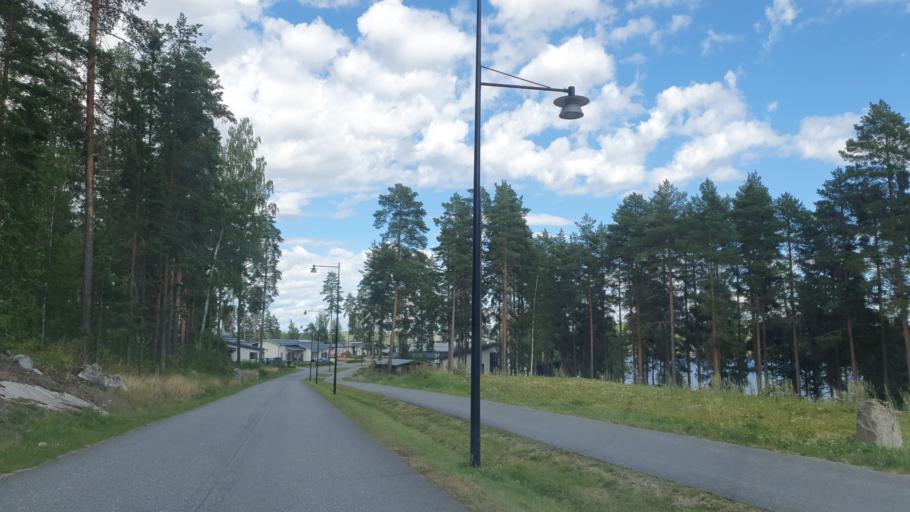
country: FI
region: Central Finland
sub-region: Jyvaeskylae
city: Saeynaetsalo
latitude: 62.1602
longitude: 25.7659
